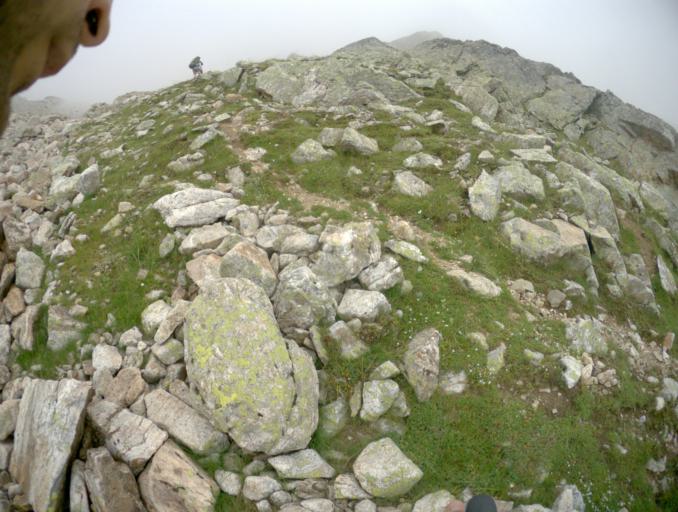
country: RU
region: Karachayevo-Cherkesiya
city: Uchkulan
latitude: 43.2828
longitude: 42.1030
